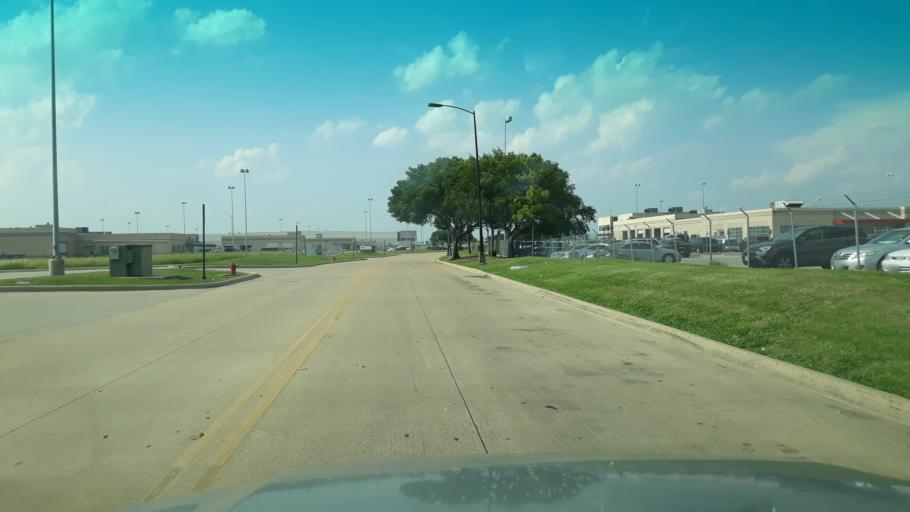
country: US
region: Texas
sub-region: Tarrant County
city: Euless
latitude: 32.8563
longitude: -97.0286
